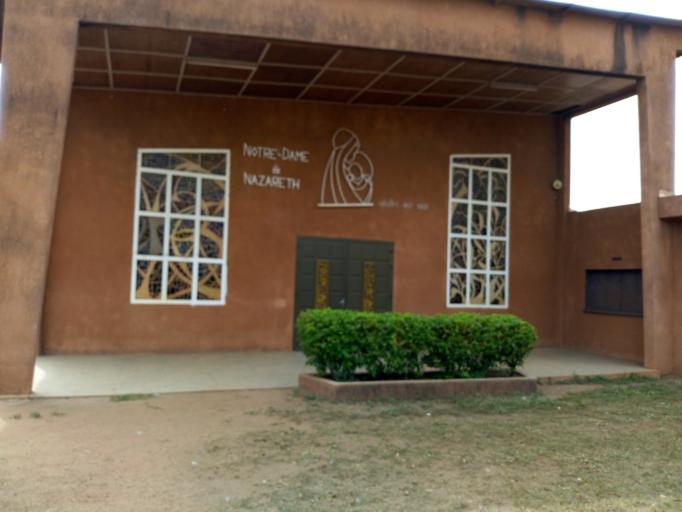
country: CI
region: Vallee du Bandama
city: Bouake
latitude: 7.7055
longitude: -5.0284
